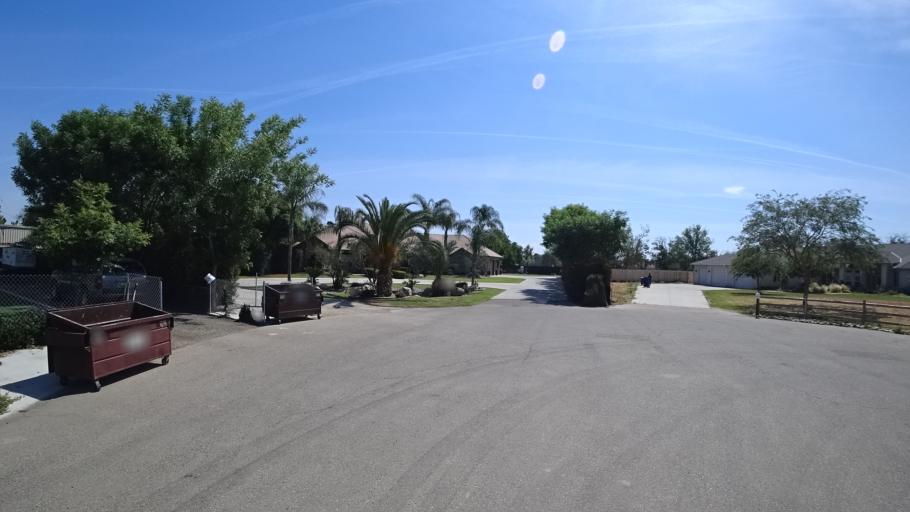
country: US
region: California
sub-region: Kings County
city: Armona
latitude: 36.3414
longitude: -119.7083
